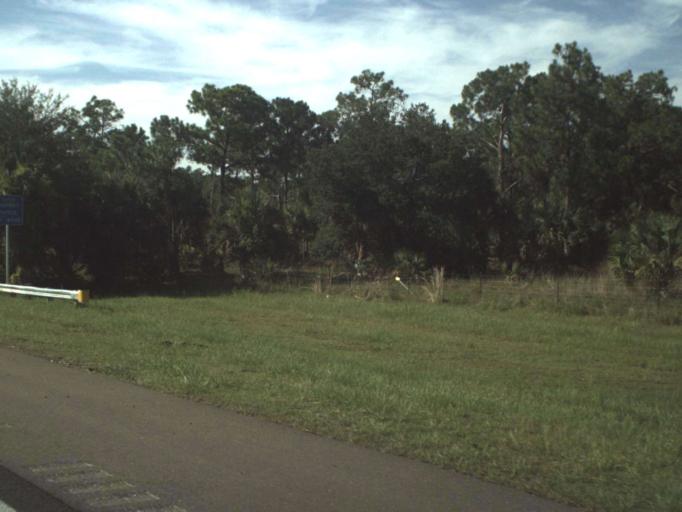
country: US
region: Florida
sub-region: Indian River County
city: Roseland
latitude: 27.8225
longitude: -80.5551
